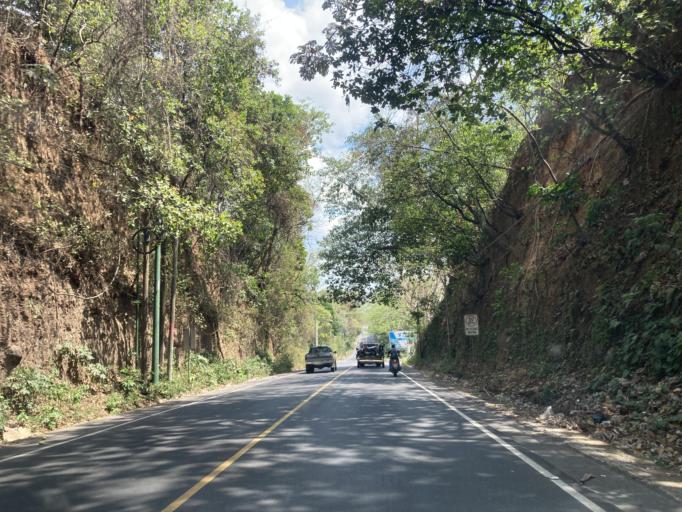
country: GT
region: Santa Rosa
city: Guazacapan
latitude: 14.0700
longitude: -90.4321
